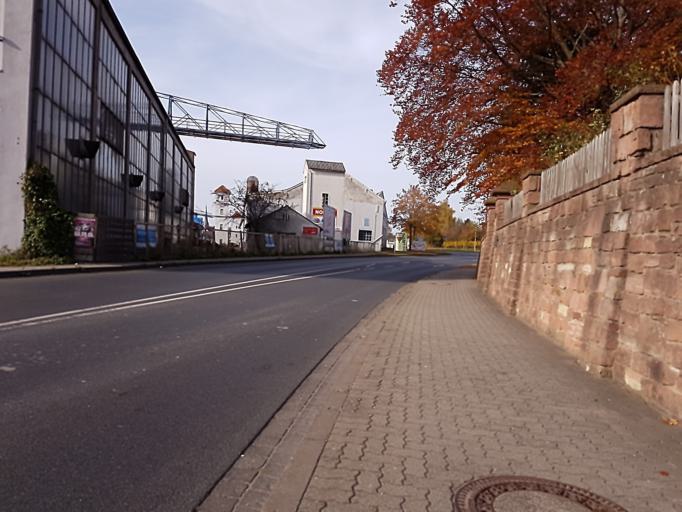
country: DE
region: Bavaria
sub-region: Regierungsbezirk Unterfranken
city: Erlenbach am Main
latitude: 49.7976
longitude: 9.1643
